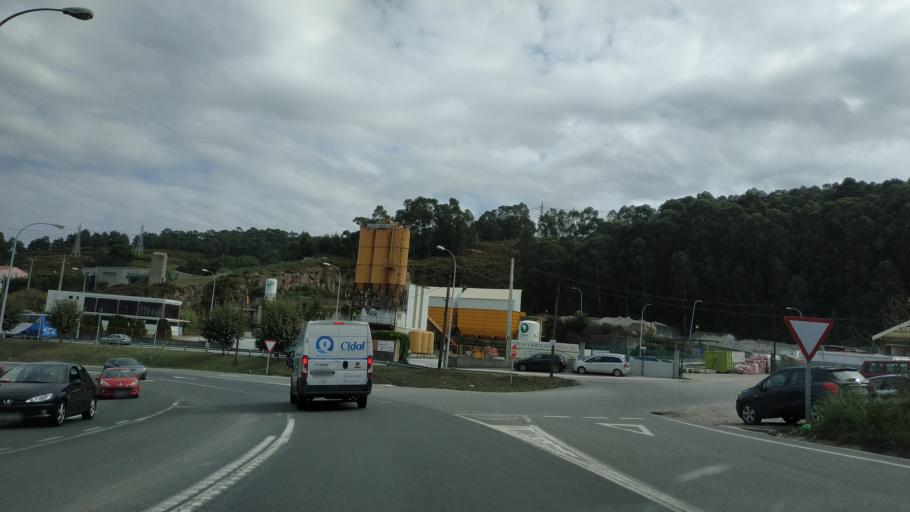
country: ES
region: Galicia
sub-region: Provincia da Coruna
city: A Coruna
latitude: 43.3391
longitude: -8.4471
